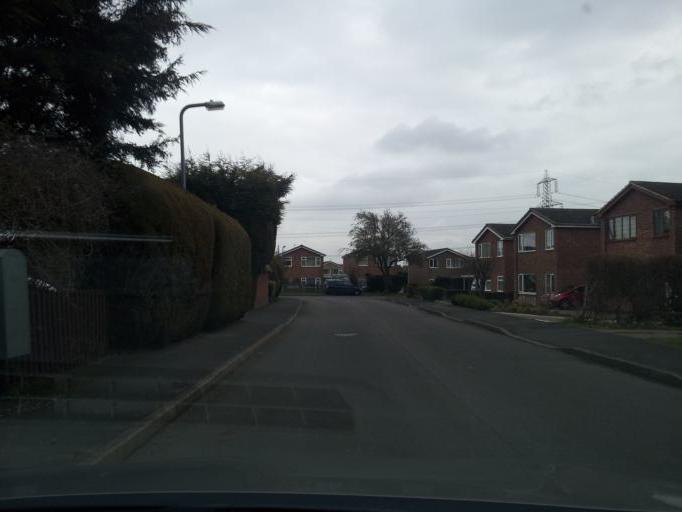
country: GB
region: England
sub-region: Lincolnshire
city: Barrowby
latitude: 52.9133
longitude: -0.6840
